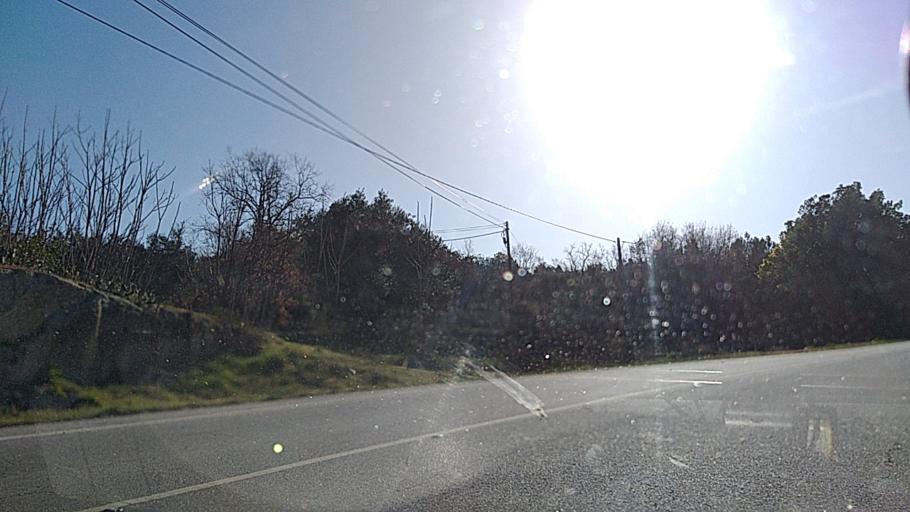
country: PT
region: Guarda
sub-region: Fornos de Algodres
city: Fornos de Algodres
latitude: 40.6180
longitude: -7.5158
